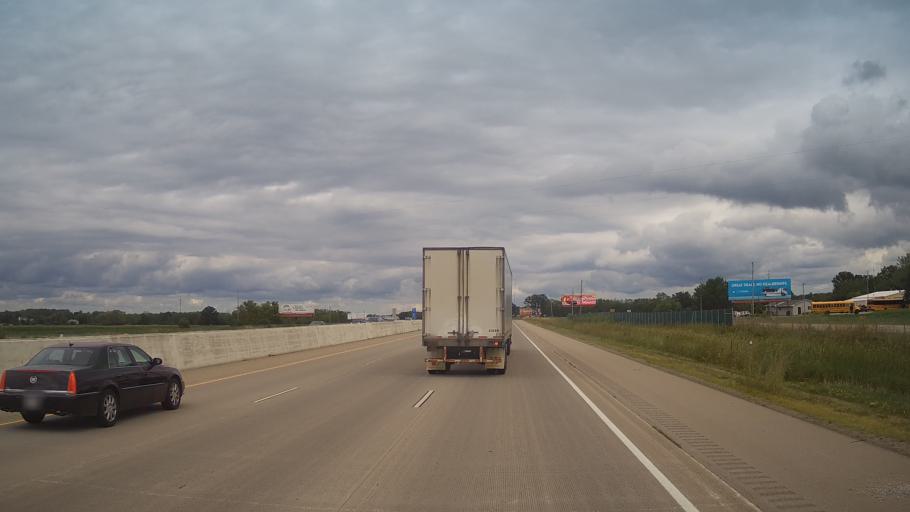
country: US
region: Wisconsin
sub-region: Winnebago County
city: Neenah
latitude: 44.1187
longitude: -88.5090
